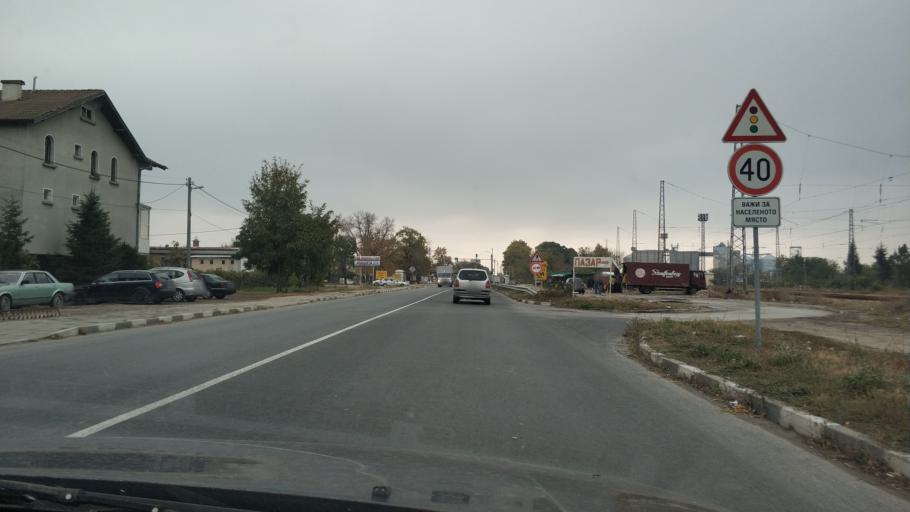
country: BG
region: Plovdiv
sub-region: Obshtina Plovdiv
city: Plovdiv
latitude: 42.2325
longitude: 24.7240
